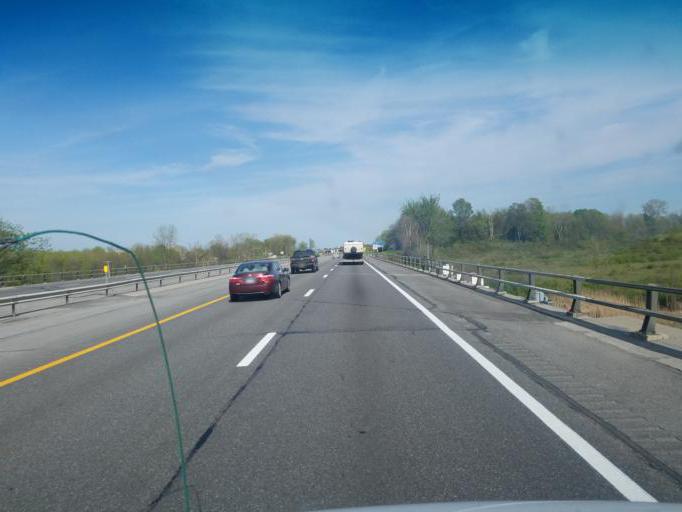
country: US
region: New York
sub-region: Oneida County
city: Sherrill
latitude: 43.1260
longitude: -75.5998
